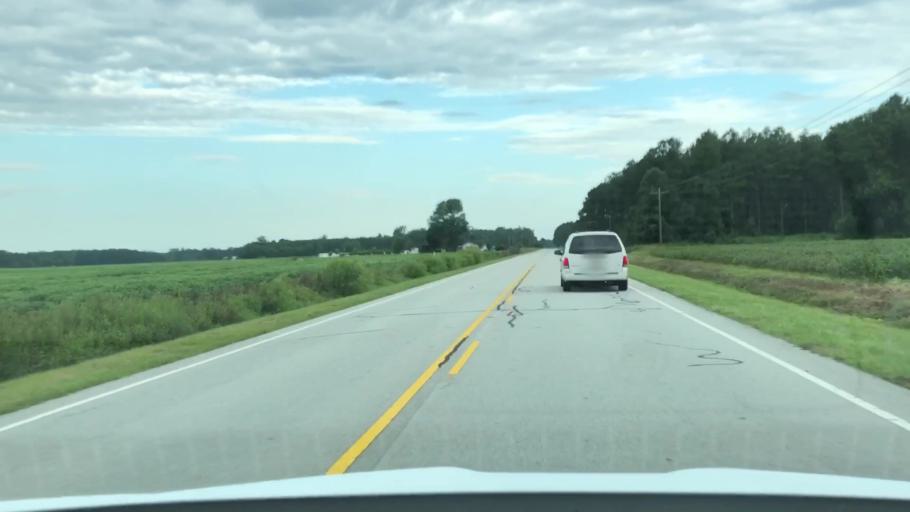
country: US
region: North Carolina
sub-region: Jones County
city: Trenton
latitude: 35.0800
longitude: -77.4316
